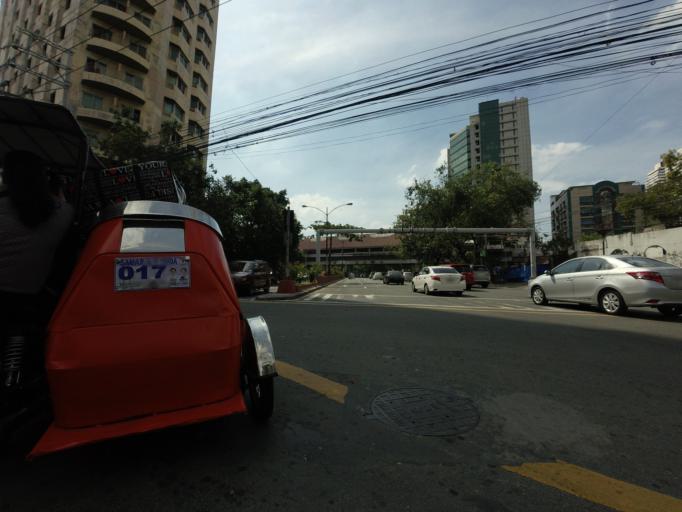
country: PH
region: Metro Manila
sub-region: City of Manila
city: Port Area
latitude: 14.5711
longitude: 120.9922
